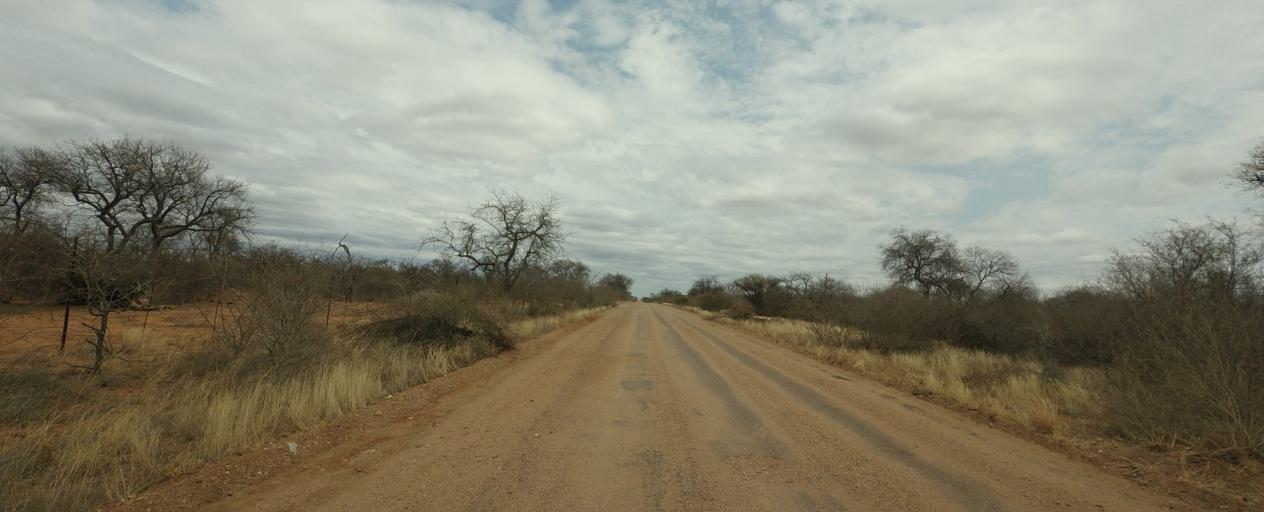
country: BW
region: Central
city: Mathathane
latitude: -22.6717
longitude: 28.6811
